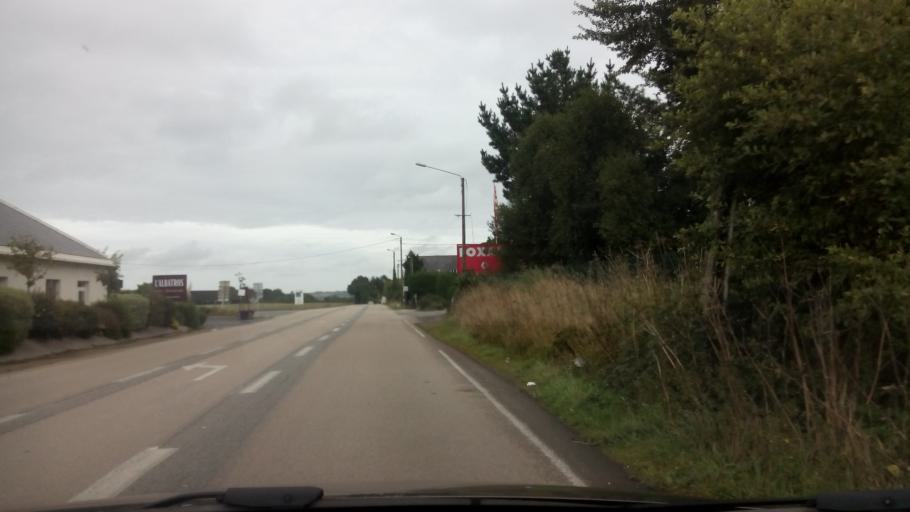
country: FR
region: Brittany
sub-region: Departement du Finistere
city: Morlaix
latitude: 48.5961
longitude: -3.8142
